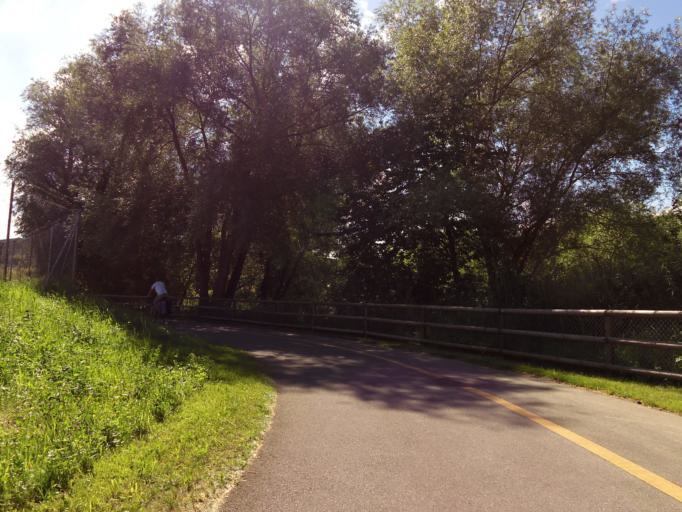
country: CH
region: Thurgau
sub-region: Arbon District
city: Arbon
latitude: 47.5197
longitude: 9.4305
